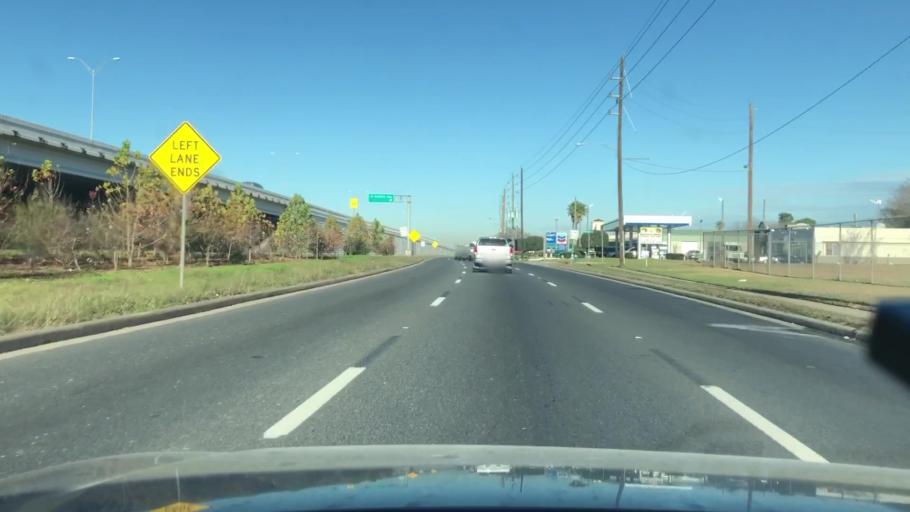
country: US
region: Texas
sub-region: Fort Bend County
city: Missouri City
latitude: 29.6450
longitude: -95.5394
